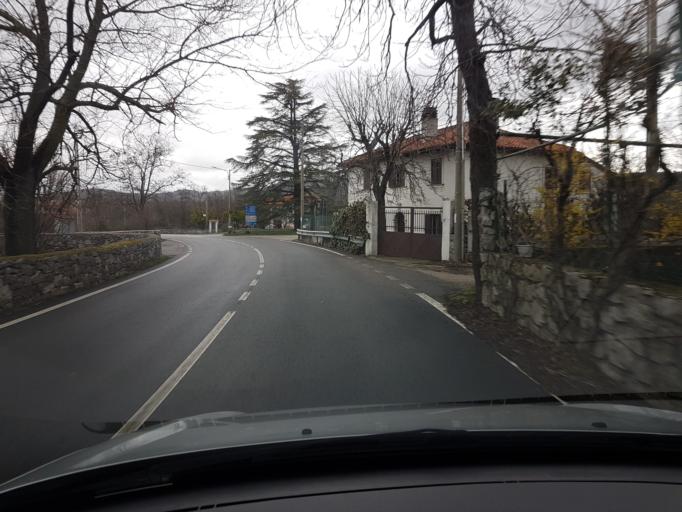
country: IT
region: Friuli Venezia Giulia
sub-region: Provincia di Trieste
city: Sgonico
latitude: 45.7462
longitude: 13.7223
